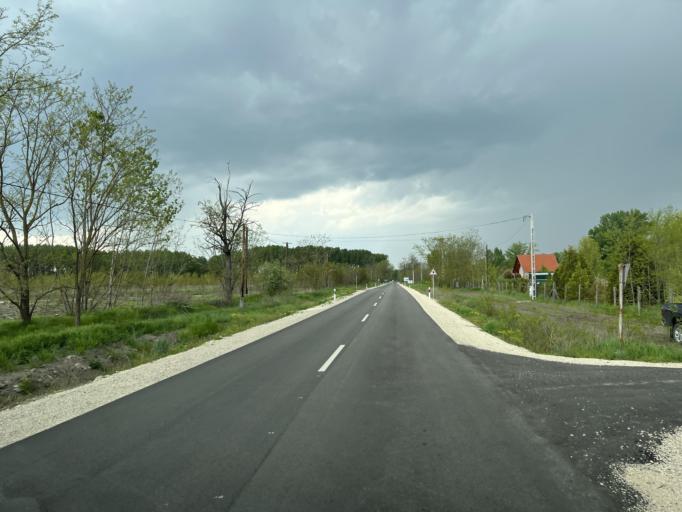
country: HU
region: Pest
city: Nagykoros
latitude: 47.0510
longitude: 19.7262
